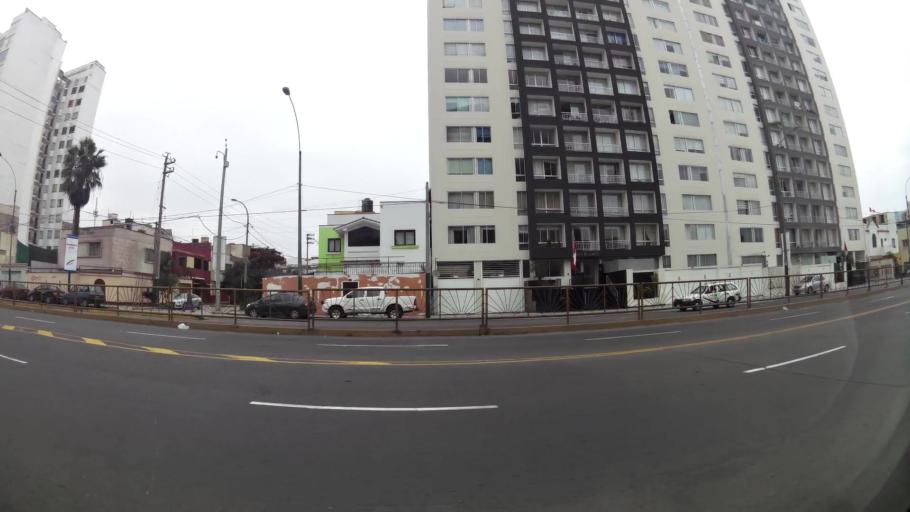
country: PE
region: Lima
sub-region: Lima
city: San Isidro
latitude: -12.0879
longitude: -77.0644
